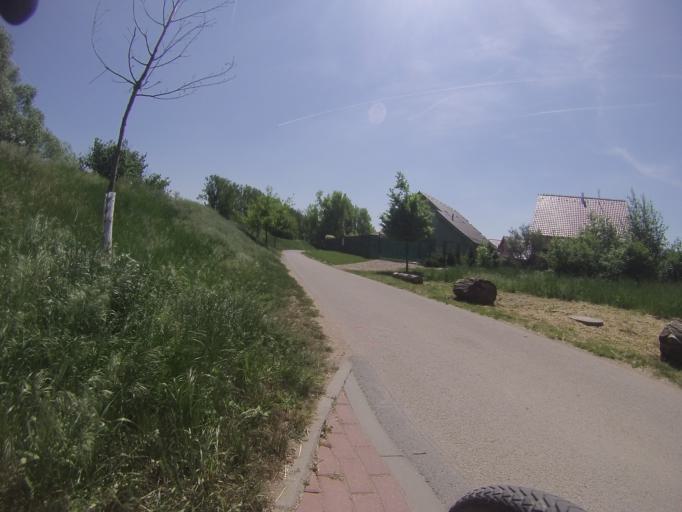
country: CZ
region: South Moravian
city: Zidlochovice
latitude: 49.0324
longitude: 16.6194
